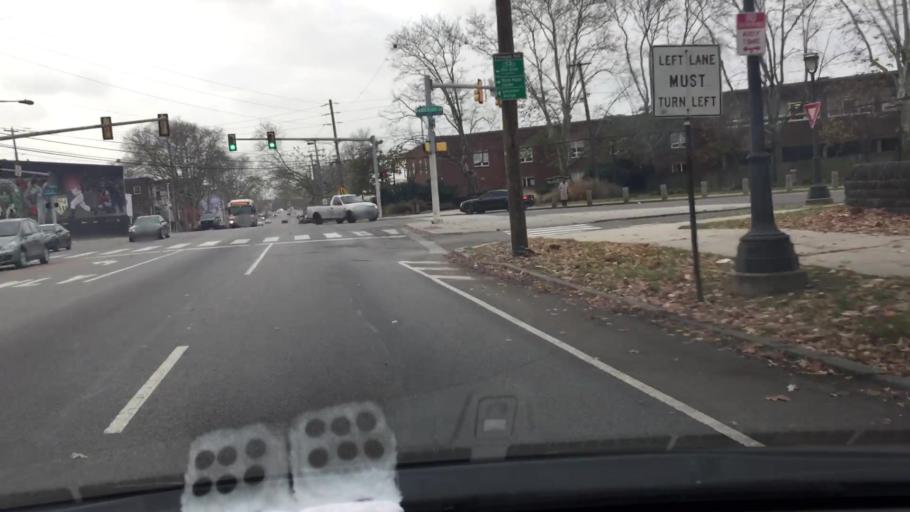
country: US
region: Pennsylvania
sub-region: Montgomery County
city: Bala-Cynwyd
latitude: 39.9789
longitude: -75.2139
